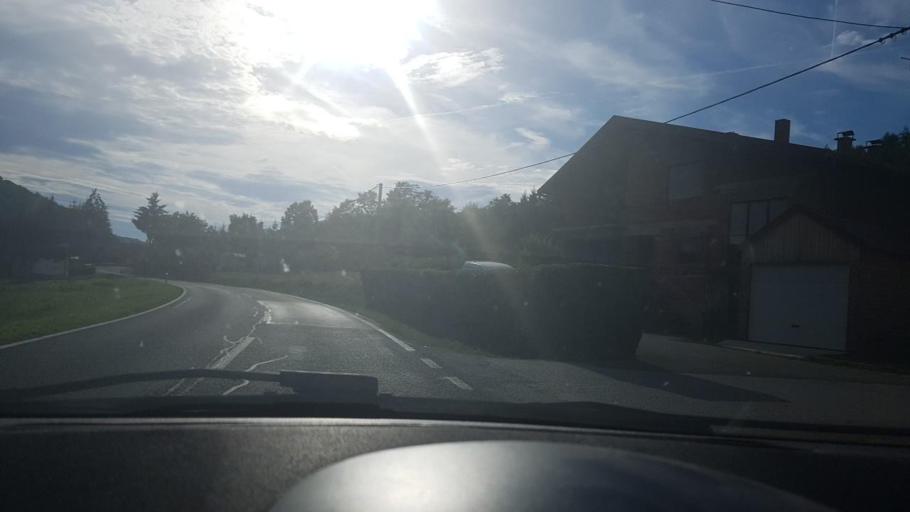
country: HR
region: Varazdinska
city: Lepoglava
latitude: 46.2132
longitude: 16.0164
